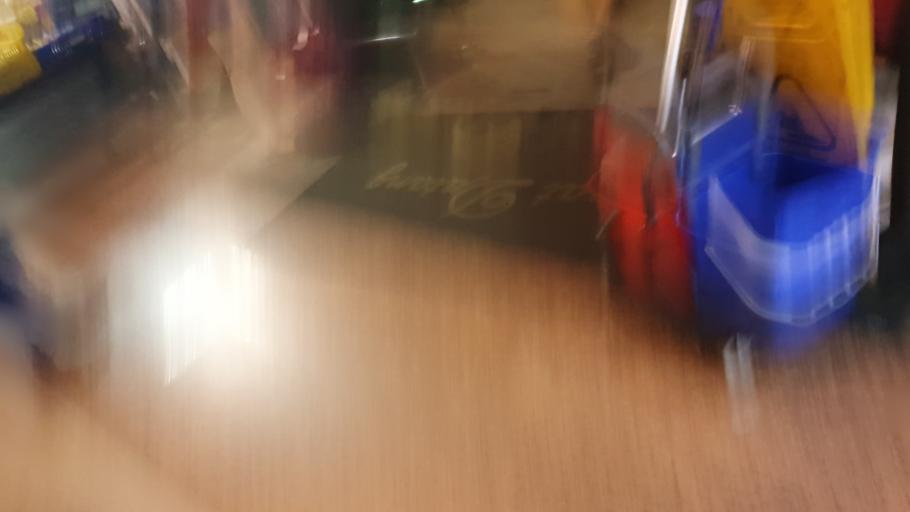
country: MY
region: Johor
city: Johor Bahru
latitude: 1.4636
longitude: 103.7645
